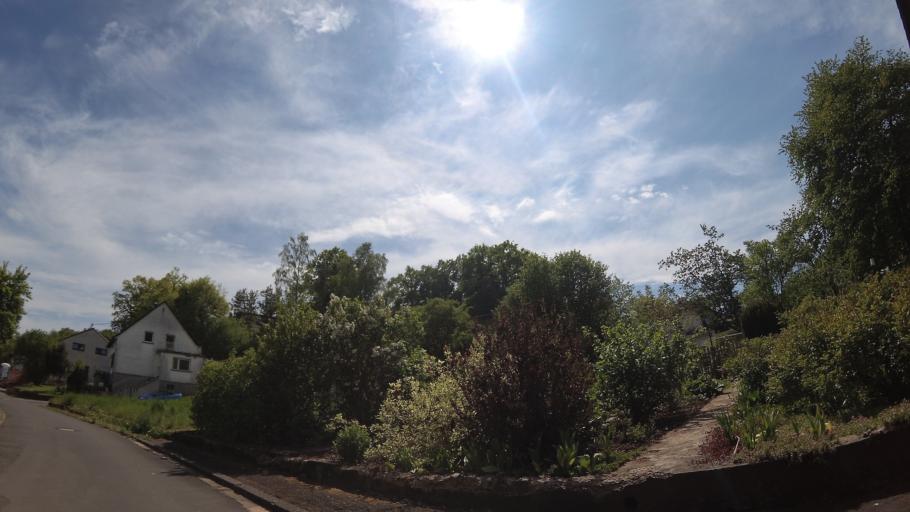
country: DE
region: Saarland
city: Sankt Wendel
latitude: 49.4933
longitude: 7.1601
